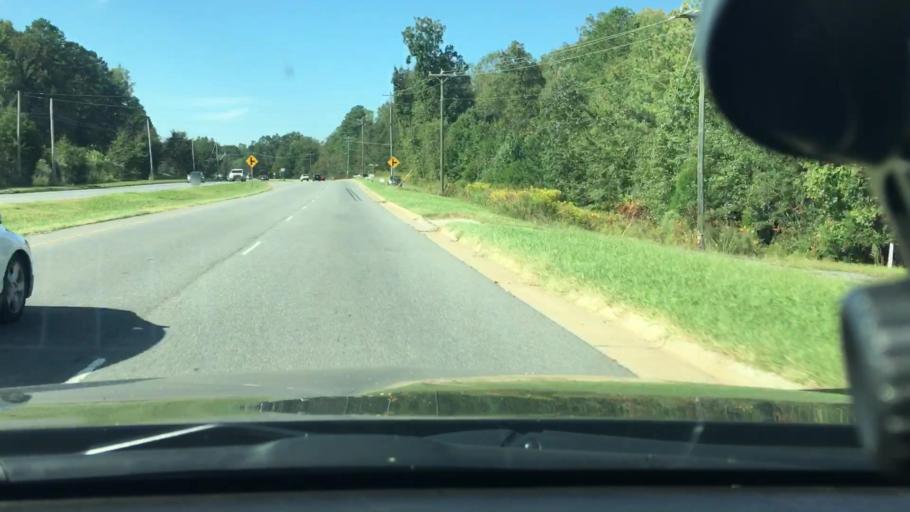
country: US
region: North Carolina
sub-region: Mecklenburg County
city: Mint Hill
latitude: 35.2331
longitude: -80.6022
